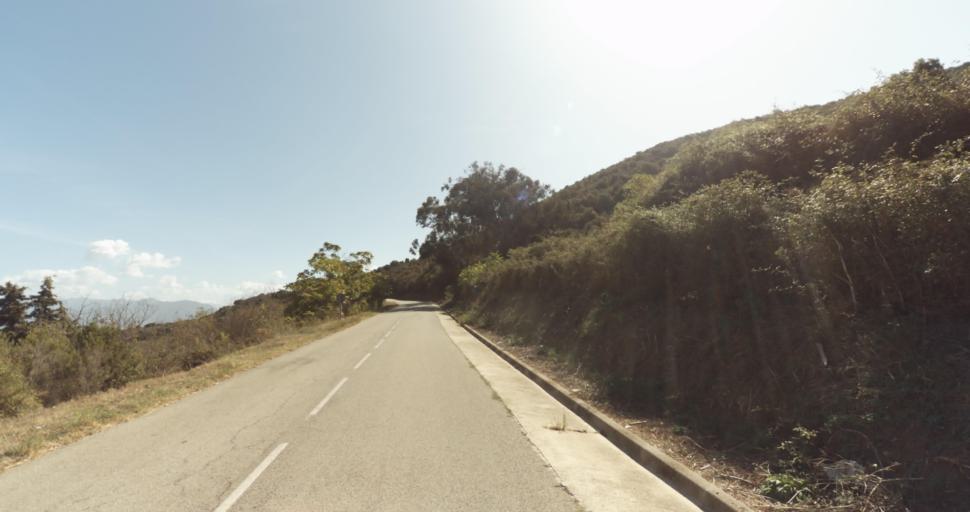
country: FR
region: Corsica
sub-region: Departement de la Corse-du-Sud
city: Ajaccio
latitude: 41.9282
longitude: 8.7027
